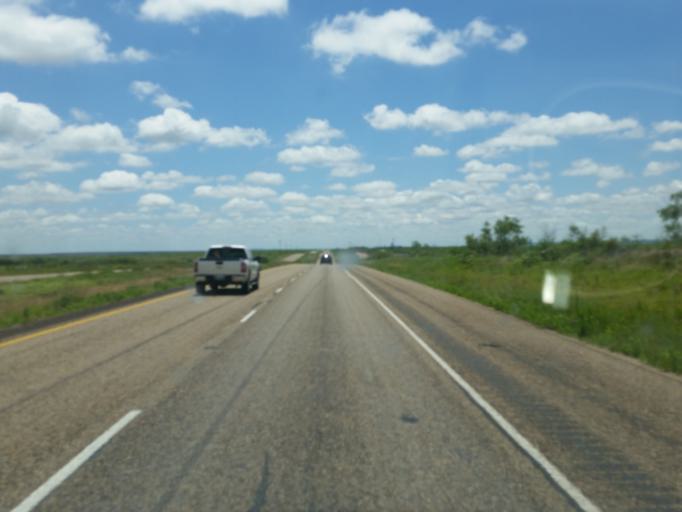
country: US
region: Texas
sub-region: Garza County
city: Post
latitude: 33.1380
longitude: -101.3128
